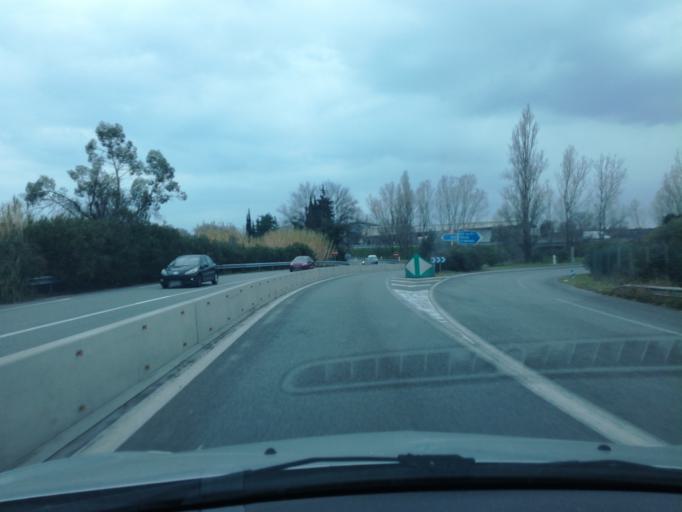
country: FR
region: Provence-Alpes-Cote d'Azur
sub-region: Departement des Alpes-Maritimes
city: Mandelieu-la-Napoule
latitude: 43.5591
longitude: 6.9547
